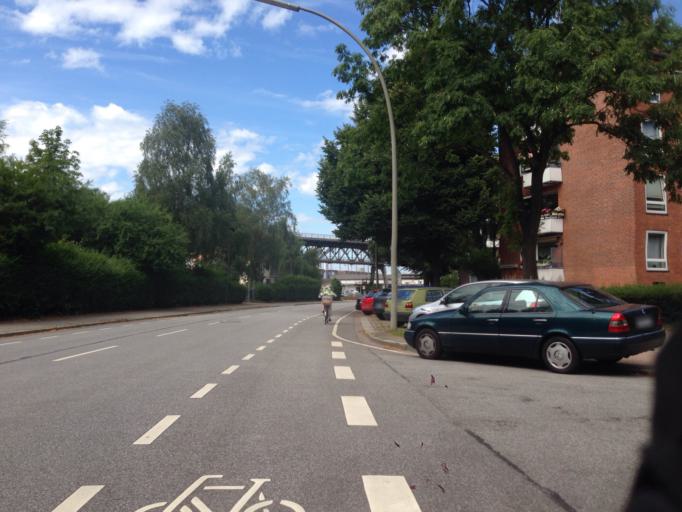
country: DE
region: Hamburg
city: Barmbek-Nord
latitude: 53.5901
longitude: 10.0396
